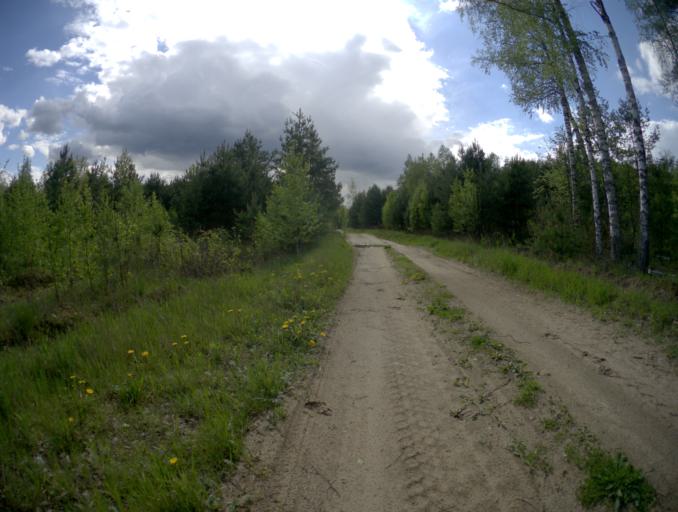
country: RU
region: Rjazan
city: Tuma
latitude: 55.2135
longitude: 40.4553
